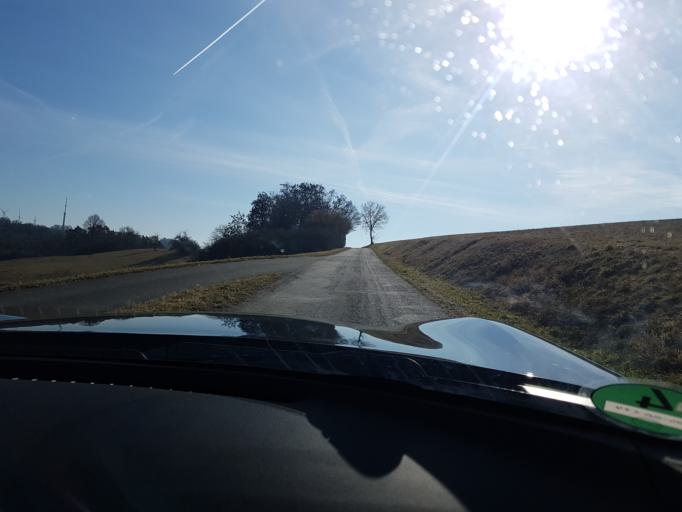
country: DE
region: Baden-Wuerttemberg
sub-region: Karlsruhe Region
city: Rosenberg
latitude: 49.4100
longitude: 9.5038
